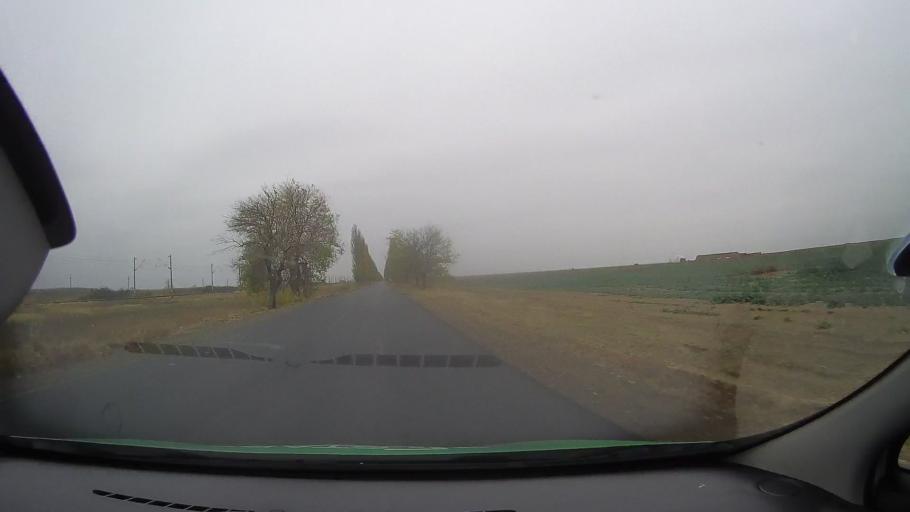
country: RO
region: Ialomita
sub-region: Comuna Valea Ciorii
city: Valea Ciorii
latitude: 44.7079
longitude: 27.5938
